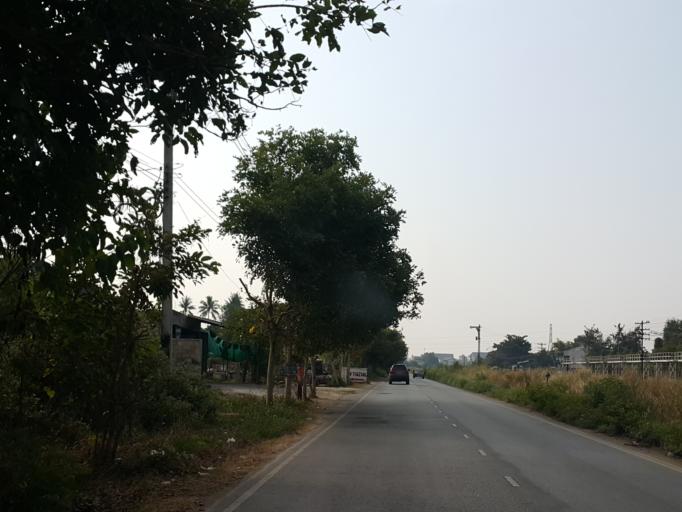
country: TH
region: Chiang Mai
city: Chiang Mai
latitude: 18.7727
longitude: 99.0173
